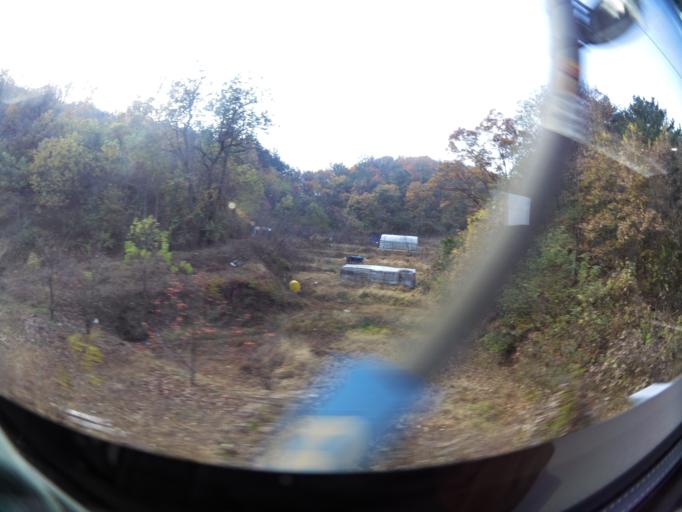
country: KR
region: Gyeongsangbuk-do
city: Gimcheon
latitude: 36.1328
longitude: 128.0219
